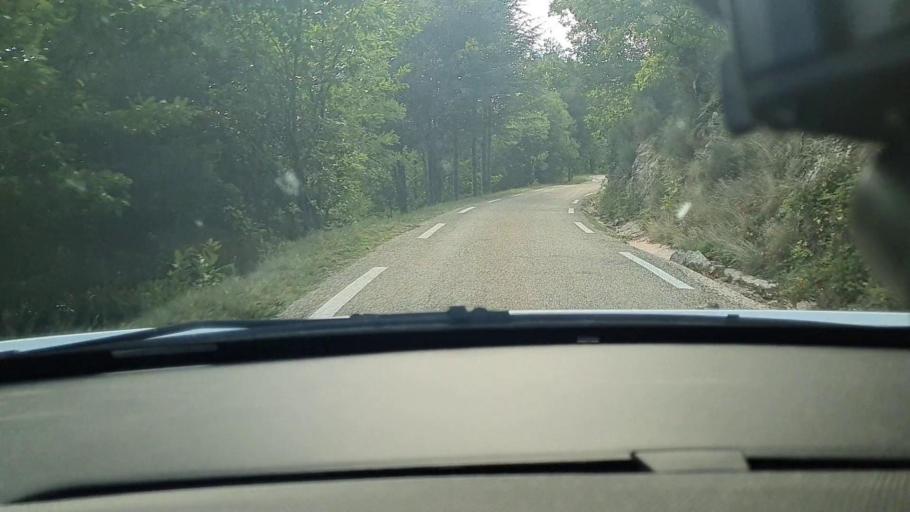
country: FR
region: Languedoc-Roussillon
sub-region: Departement du Gard
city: Branoux-les-Taillades
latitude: 44.3527
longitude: 3.9273
